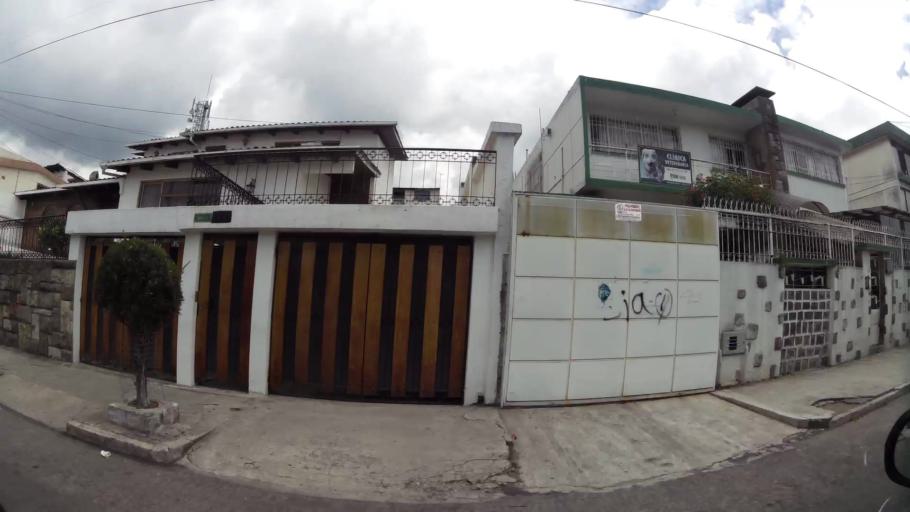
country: EC
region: Pichincha
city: Quito
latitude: -0.1833
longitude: -78.4942
